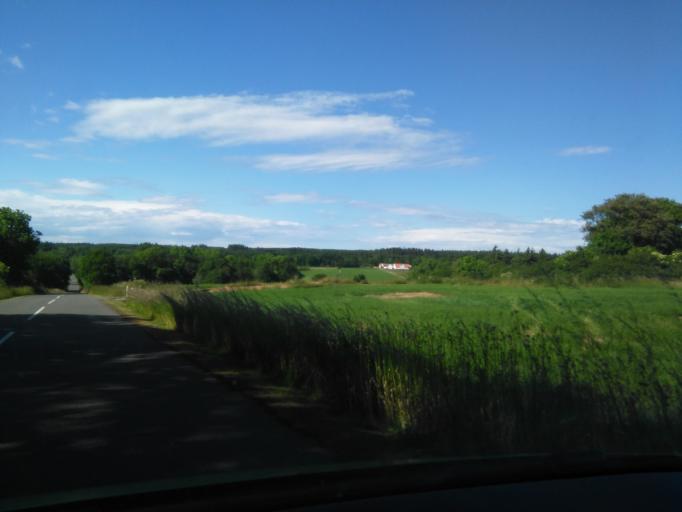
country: DK
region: Capital Region
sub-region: Bornholm Kommune
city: Nexo
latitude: 55.0737
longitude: 15.0810
